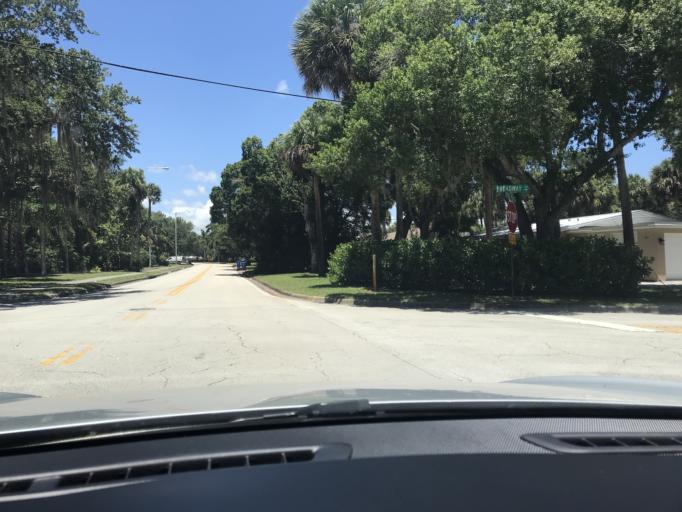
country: US
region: Florida
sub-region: Indian River County
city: Vero Beach
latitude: 27.6423
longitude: -80.3888
